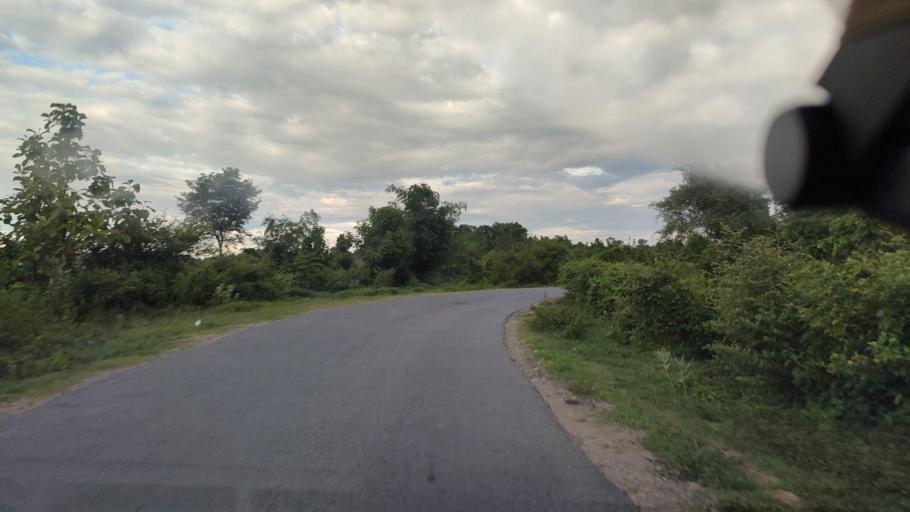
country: MM
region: Magway
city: Taungdwingyi
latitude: 20.0015
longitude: 95.8654
